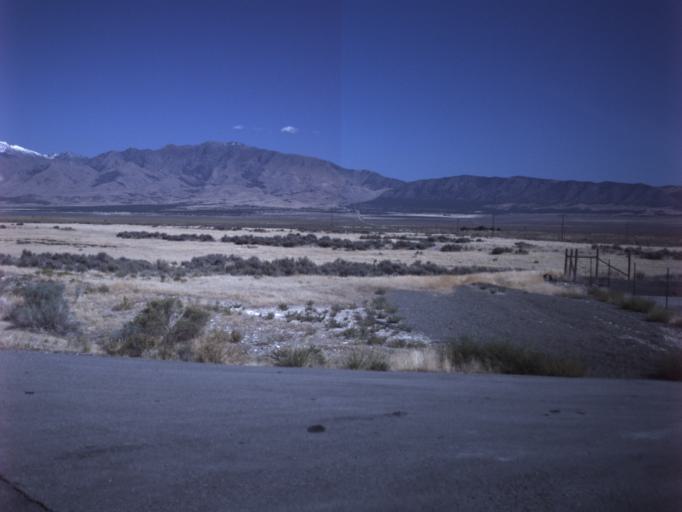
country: US
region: Utah
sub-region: Tooele County
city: Grantsville
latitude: 40.2335
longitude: -112.7233
